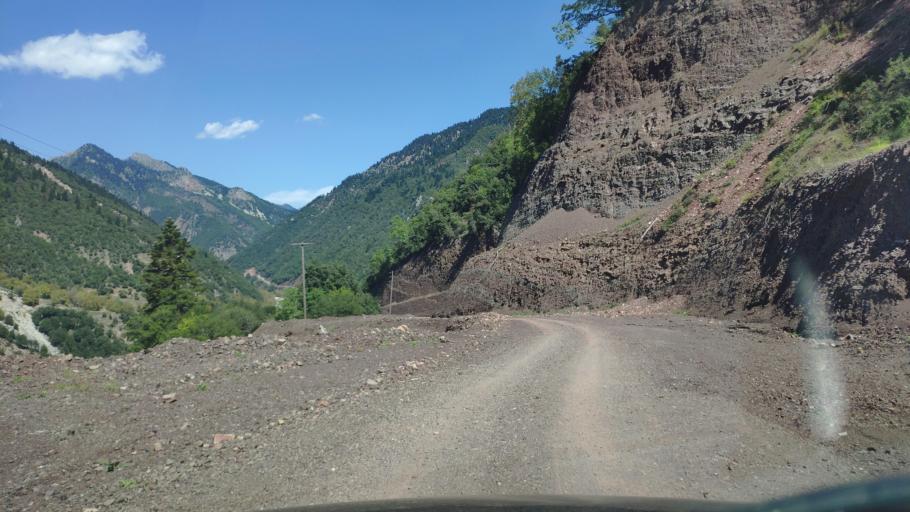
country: GR
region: Central Greece
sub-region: Nomos Evrytanias
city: Kerasochori
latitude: 39.1218
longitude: 21.6256
